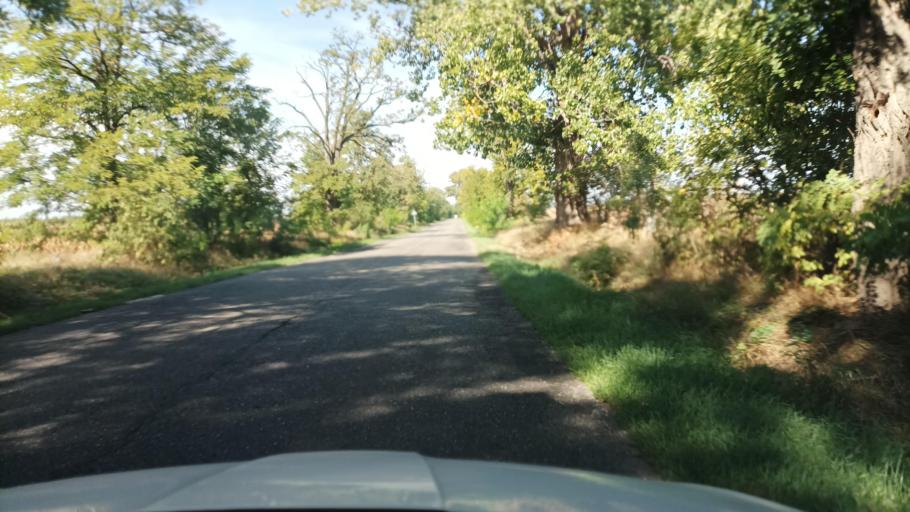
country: HU
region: Pest
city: Zsambok
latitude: 47.5537
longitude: 19.5754
